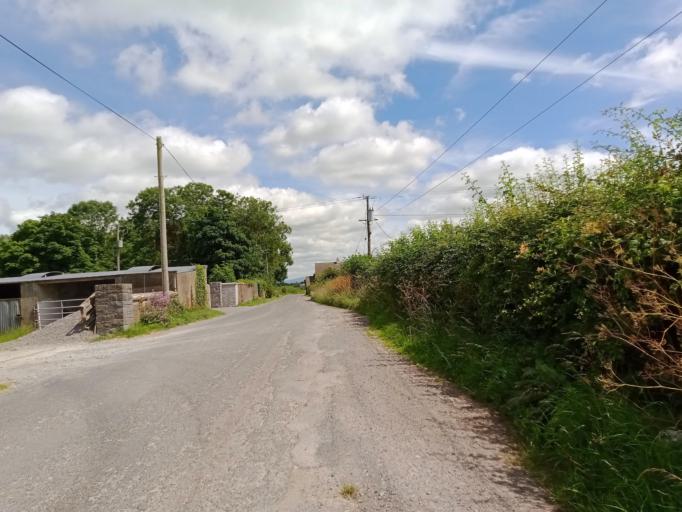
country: IE
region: Leinster
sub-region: Kilkenny
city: Callan
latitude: 52.5455
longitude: -7.4177
